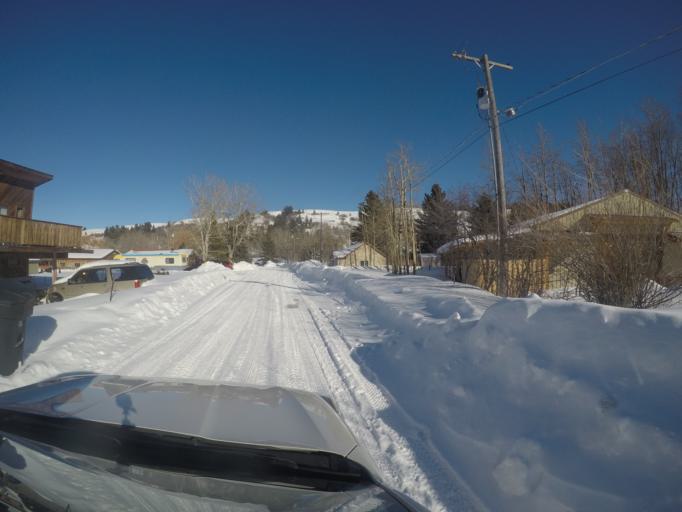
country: US
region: Montana
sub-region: Carbon County
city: Red Lodge
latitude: 45.1920
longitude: -109.2430
